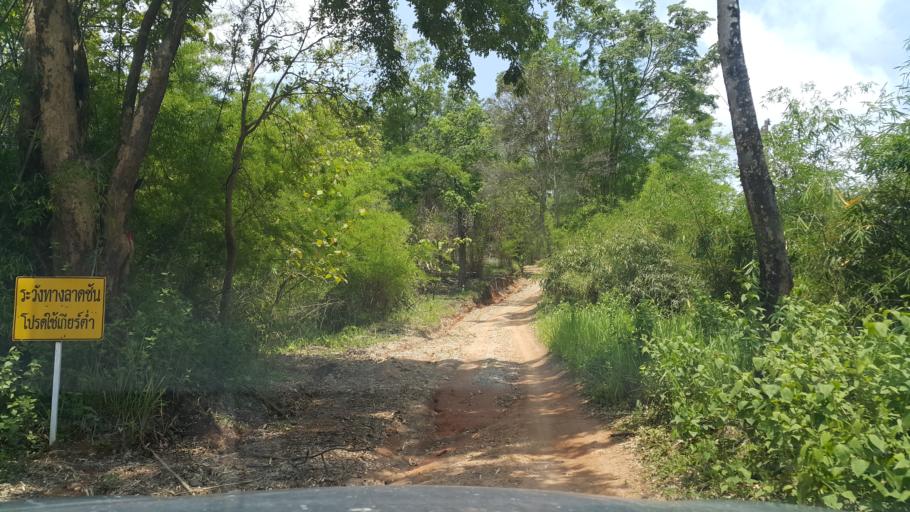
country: TH
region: Chiang Rai
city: Chiang Rai
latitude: 19.9996
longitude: 99.7164
